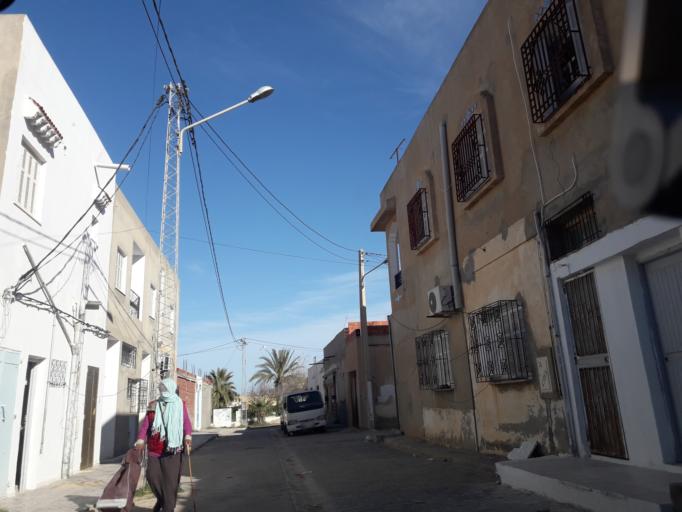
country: TN
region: Safaqis
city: Sfax
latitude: 34.7427
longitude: 10.5254
